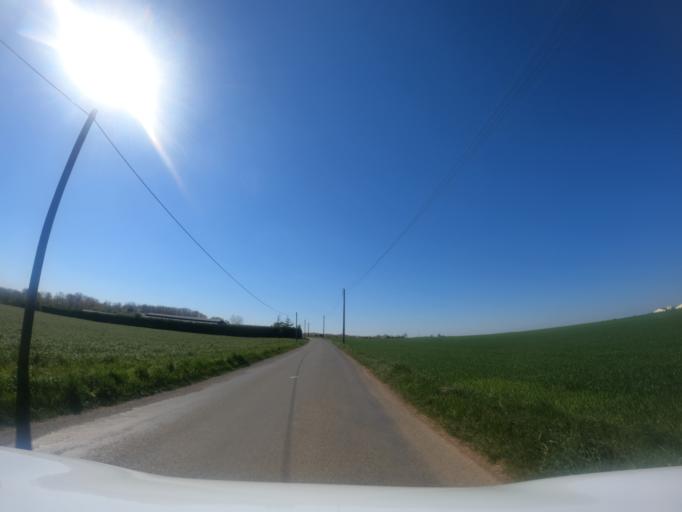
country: FR
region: Pays de la Loire
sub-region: Departement de la Vendee
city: Fontenay-le-Comte
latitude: 46.4136
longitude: -0.7925
